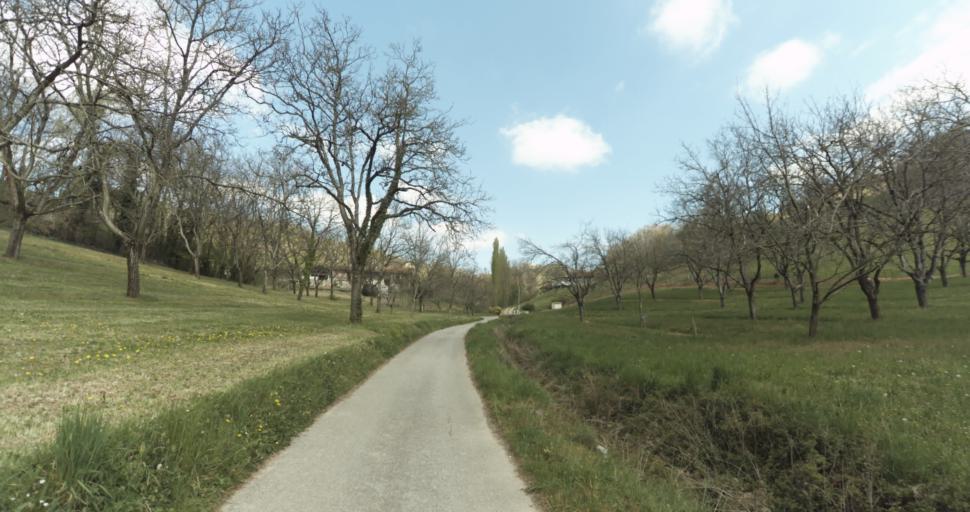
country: FR
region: Rhone-Alpes
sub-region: Departement de l'Isere
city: Saint-Verand
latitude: 45.1724
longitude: 5.3140
